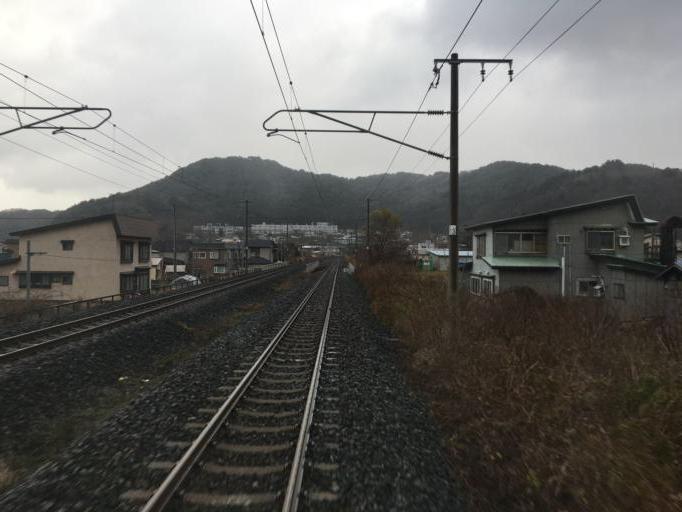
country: JP
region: Aomori
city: Aomori Shi
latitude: 40.8730
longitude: 140.8469
